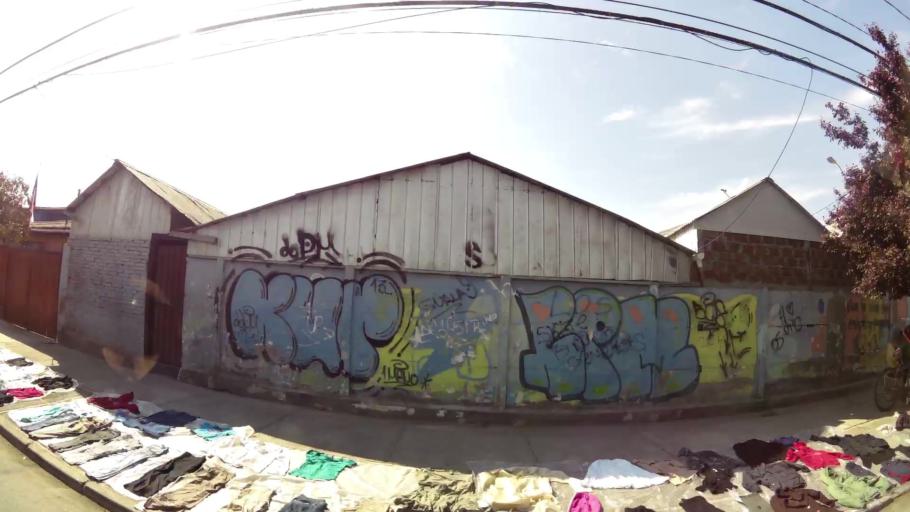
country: CL
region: Santiago Metropolitan
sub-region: Provincia de Santiago
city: La Pintana
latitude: -33.5593
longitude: -70.6604
